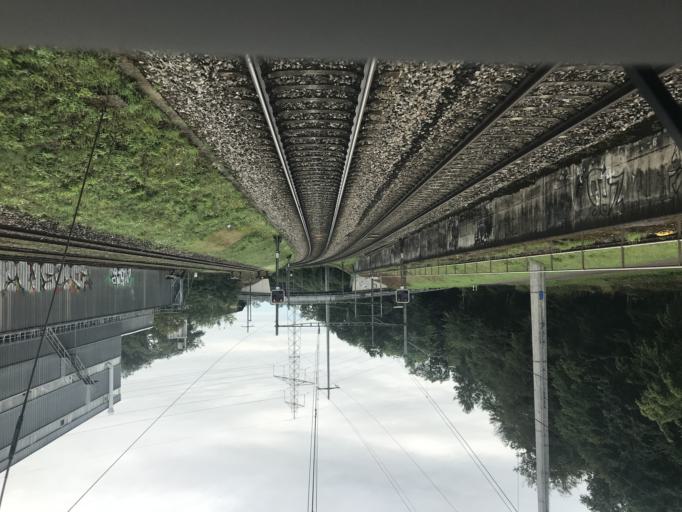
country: CH
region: Zurich
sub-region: Bezirk Buelach
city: Hochfelden
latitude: 47.5311
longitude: 8.5263
